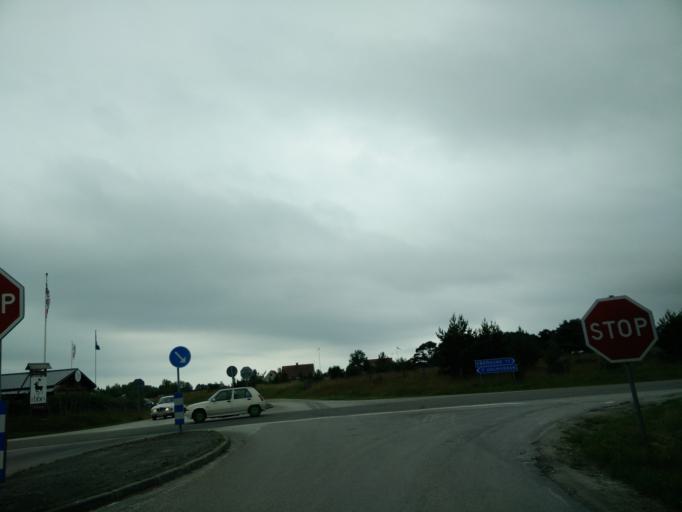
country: SE
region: Gotland
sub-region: Gotland
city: Slite
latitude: 57.9579
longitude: 19.2372
